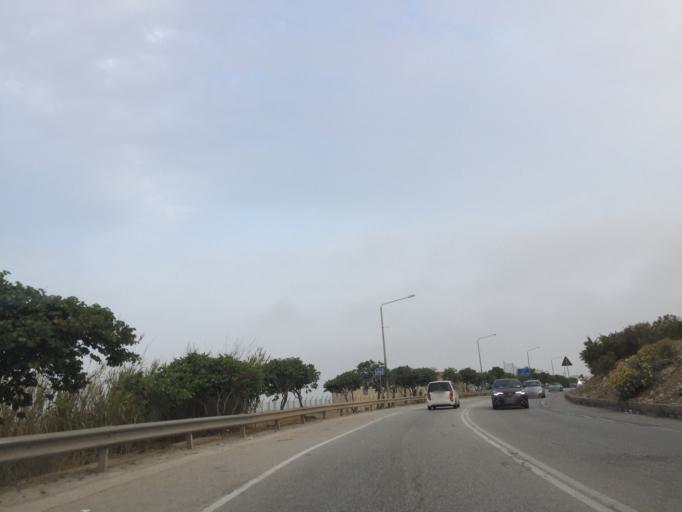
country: MT
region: Pembroke
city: Pembroke
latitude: 35.9269
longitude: 14.4720
